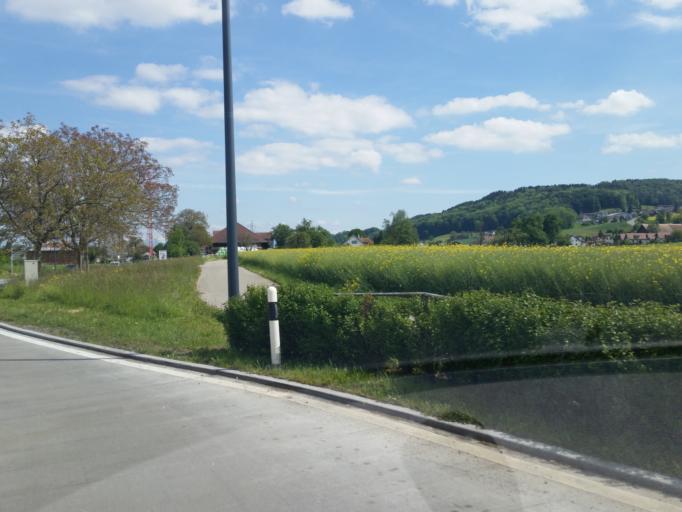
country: CH
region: Aargau
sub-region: Bezirk Bremgarten
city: Wohlen
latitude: 47.3425
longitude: 8.2690
